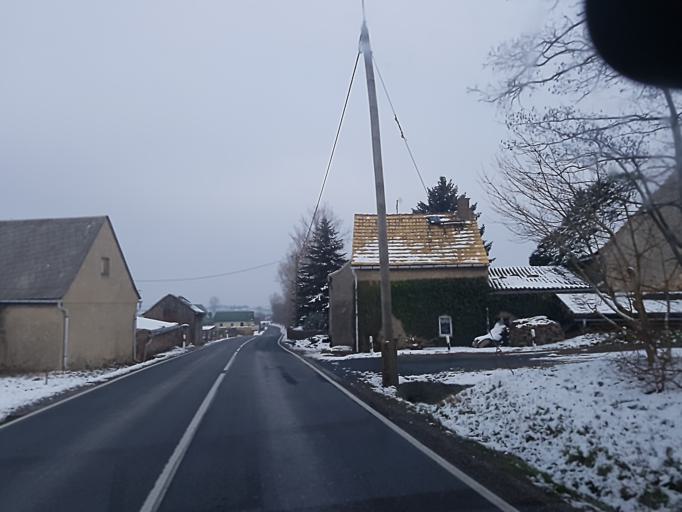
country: DE
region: Saxony
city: Bockelwitz
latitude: 51.2037
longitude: 12.9794
